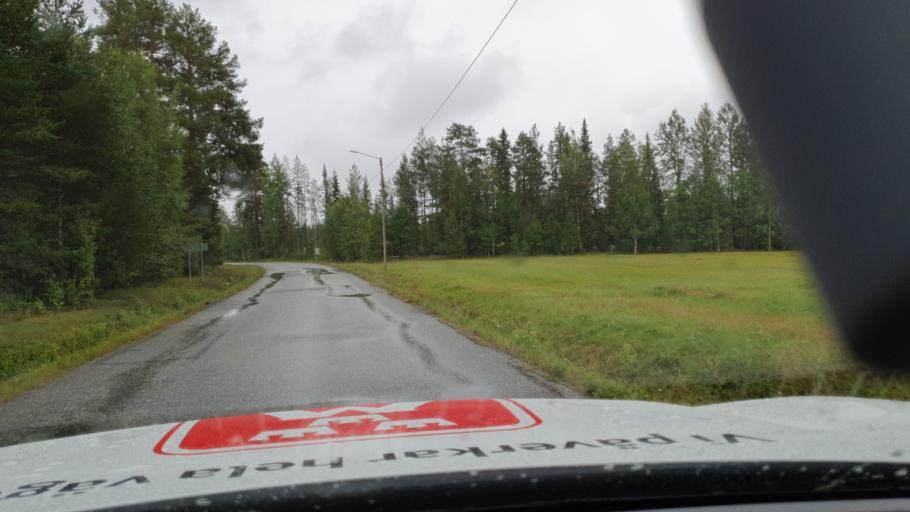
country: SE
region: Vaesterbotten
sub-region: Dorotea Kommun
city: Dorotea
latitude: 64.1079
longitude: 16.3303
